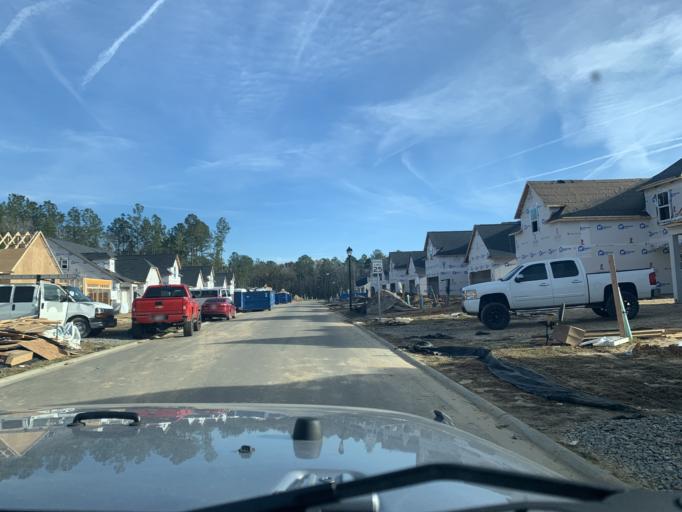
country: US
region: Georgia
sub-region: Chatham County
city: Pooler
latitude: 32.0677
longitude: -81.2566
